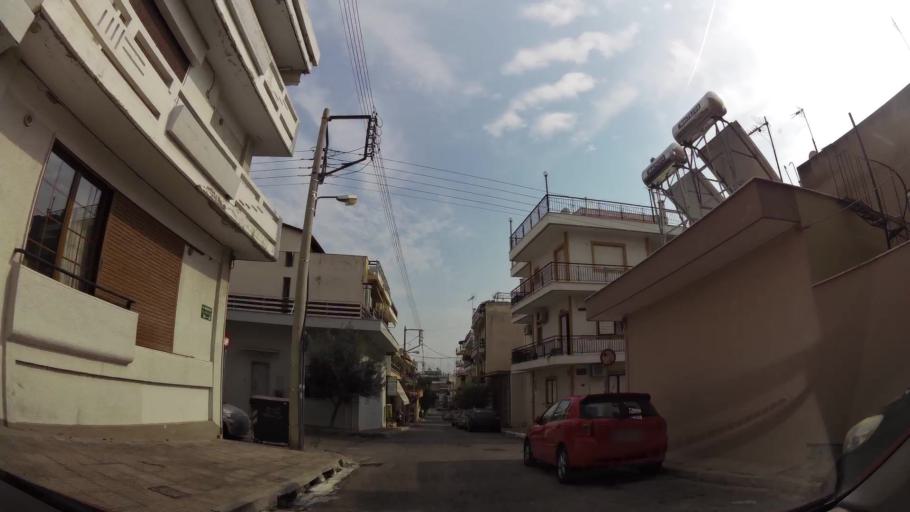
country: GR
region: Attica
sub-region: Nomarchia Athinas
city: Chaidari
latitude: 38.0106
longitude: 23.6749
